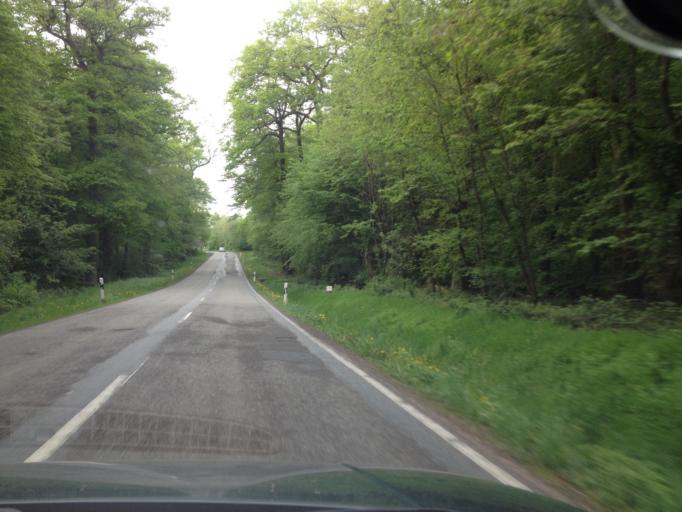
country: DE
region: Saarland
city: Mainzweiler
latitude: 49.3975
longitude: 7.1092
